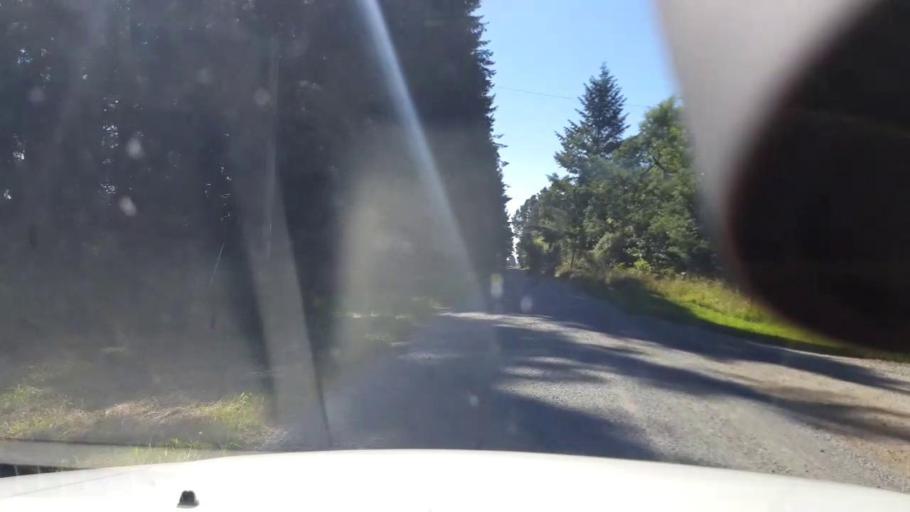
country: NZ
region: Canterbury
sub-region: Timaru District
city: Pleasant Point
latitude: -43.9676
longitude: 171.2270
